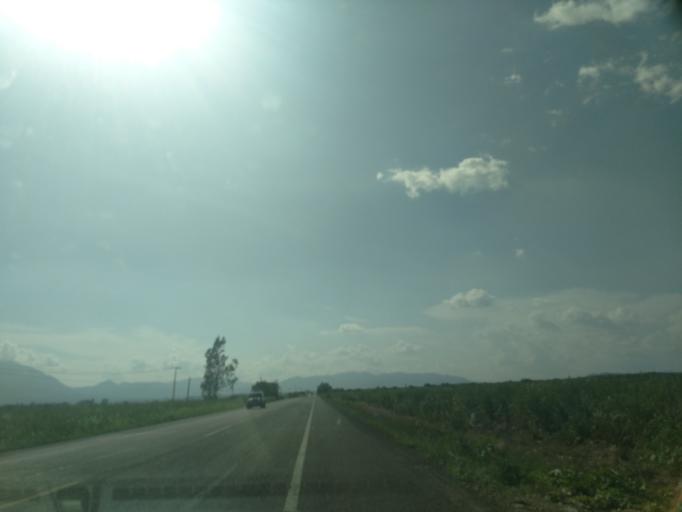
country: MX
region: Jalisco
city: Teuchitlan
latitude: 20.6826
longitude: -103.8596
